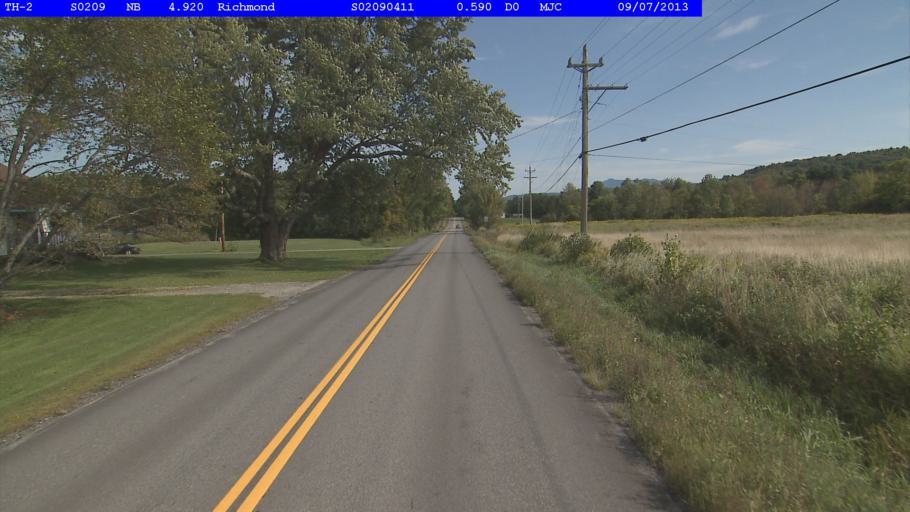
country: US
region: Vermont
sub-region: Chittenden County
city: Williston
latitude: 44.3790
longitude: -73.0594
